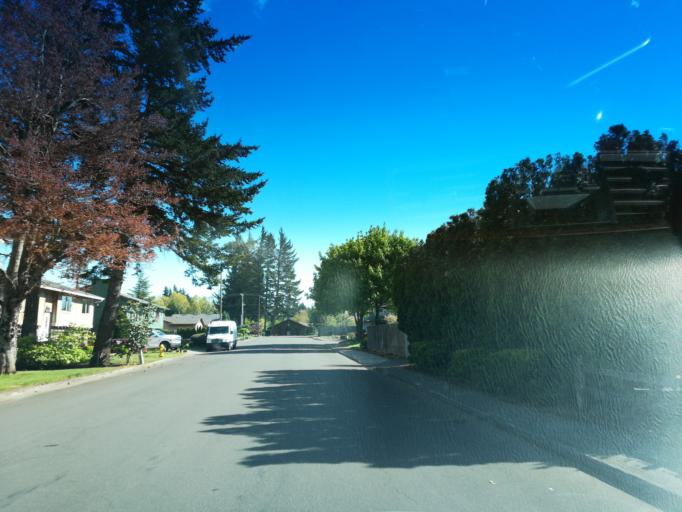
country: US
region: Oregon
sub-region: Multnomah County
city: Troutdale
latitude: 45.5351
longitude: -122.3918
